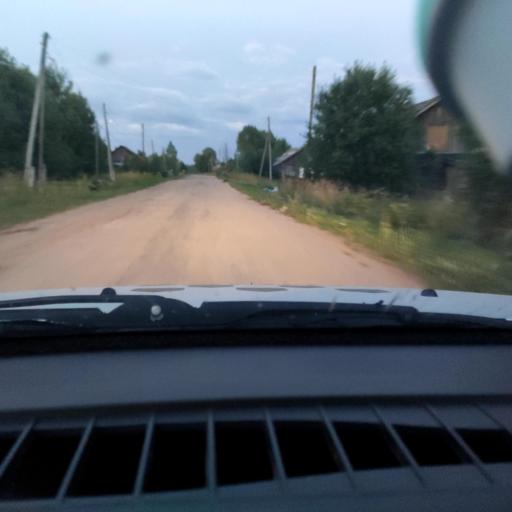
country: RU
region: Kirov
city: Darovskoy
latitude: 58.9896
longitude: 47.8682
